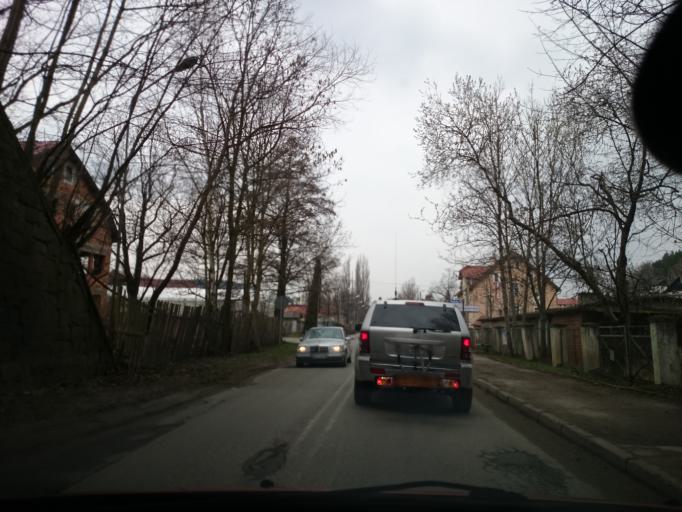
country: PL
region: Lower Silesian Voivodeship
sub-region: Powiat klodzki
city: Polanica-Zdroj
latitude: 50.3979
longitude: 16.5173
